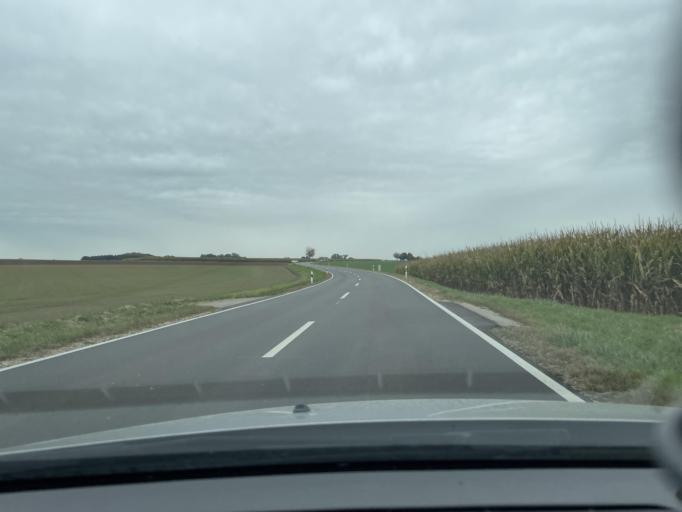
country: DE
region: Bavaria
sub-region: Upper Bavaria
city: Haimhausen
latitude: 48.3285
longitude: 11.5336
